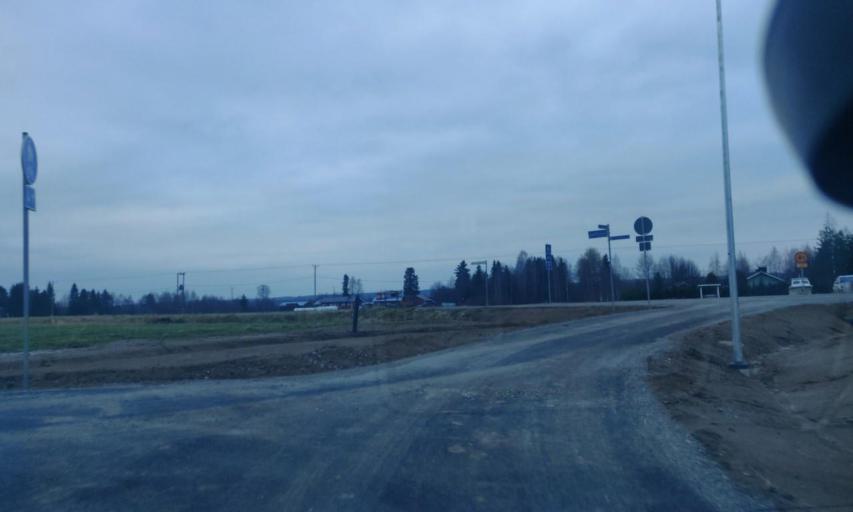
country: FI
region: Northern Ostrobothnia
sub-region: Oulu
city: Muhos
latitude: 64.7930
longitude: 26.0775
